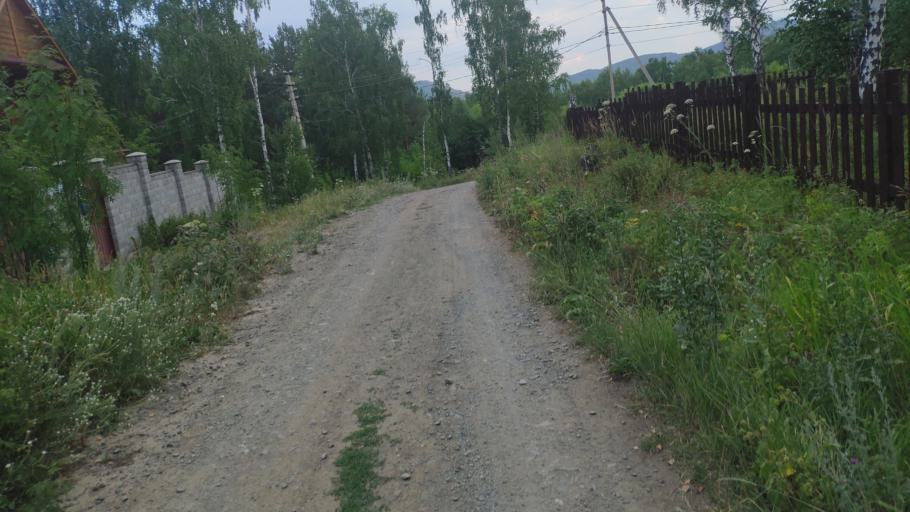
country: RU
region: Bashkortostan
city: Abzakovo
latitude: 53.8028
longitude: 58.6468
